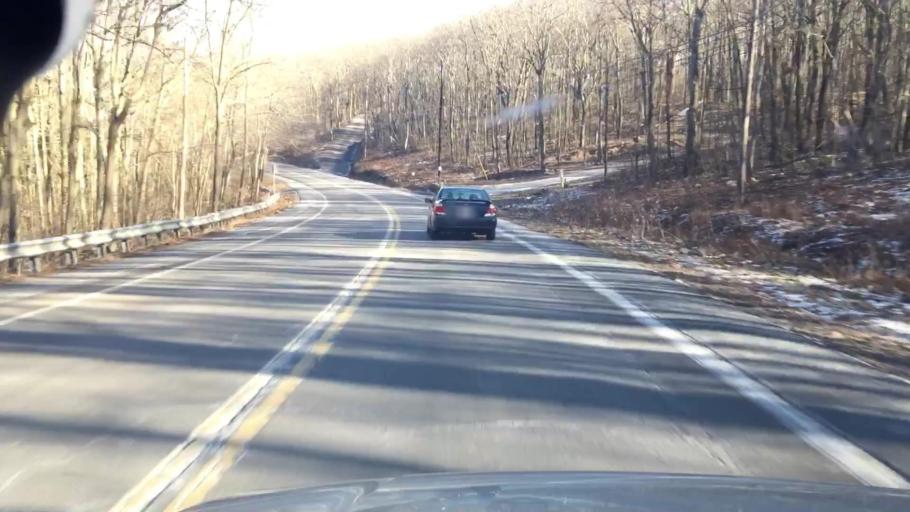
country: US
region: Pennsylvania
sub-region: Luzerne County
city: Freeland
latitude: 41.0247
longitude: -75.8649
